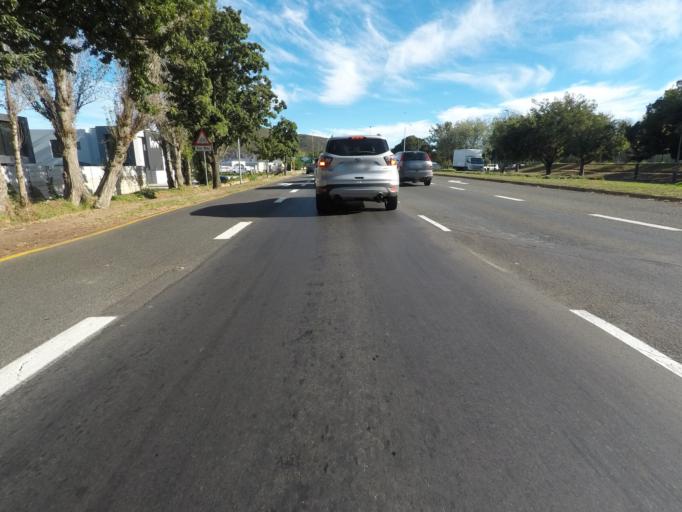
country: ZA
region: Western Cape
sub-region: Cape Winelands District Municipality
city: Stellenbosch
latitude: -33.9454
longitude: 18.8529
